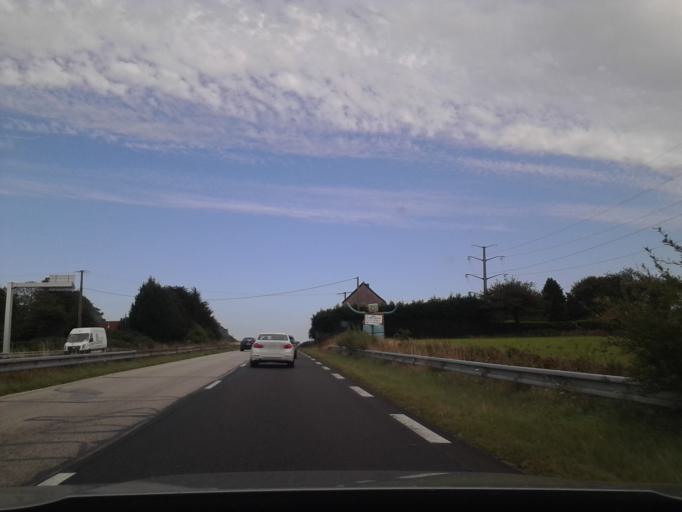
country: FR
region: Lower Normandy
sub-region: Departement de la Manche
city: La Glacerie
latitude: 49.5845
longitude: -1.5932
